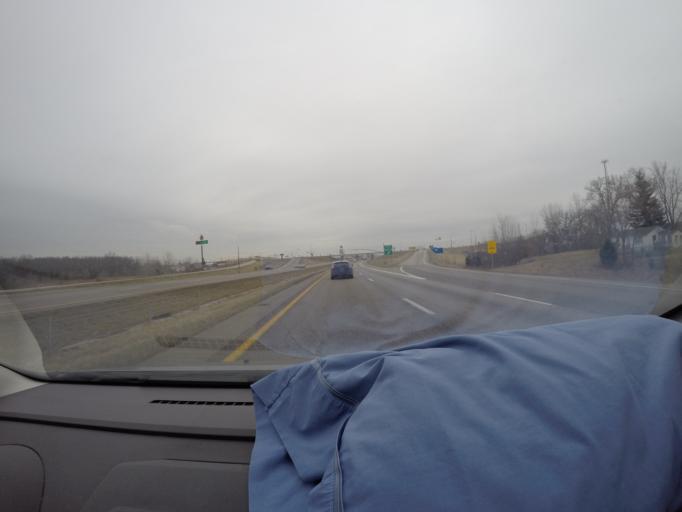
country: US
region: Missouri
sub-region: Warren County
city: Wright City
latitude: 38.8171
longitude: -90.9572
